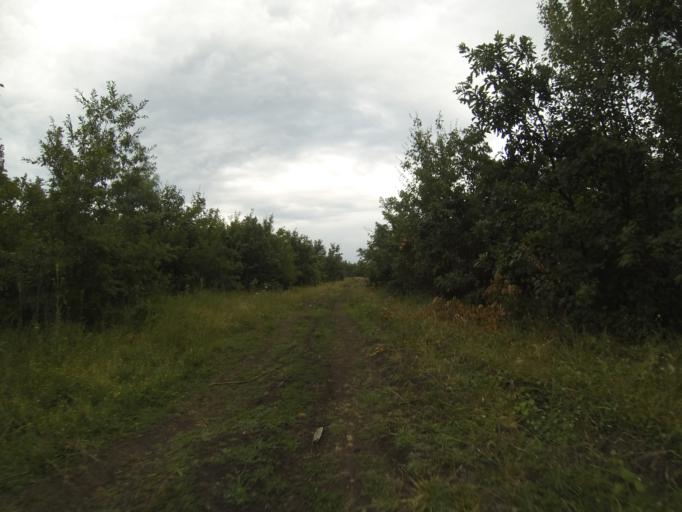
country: RO
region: Dolj
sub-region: Comuna Filiasi
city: Fratostita
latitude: 44.5799
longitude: 23.6115
